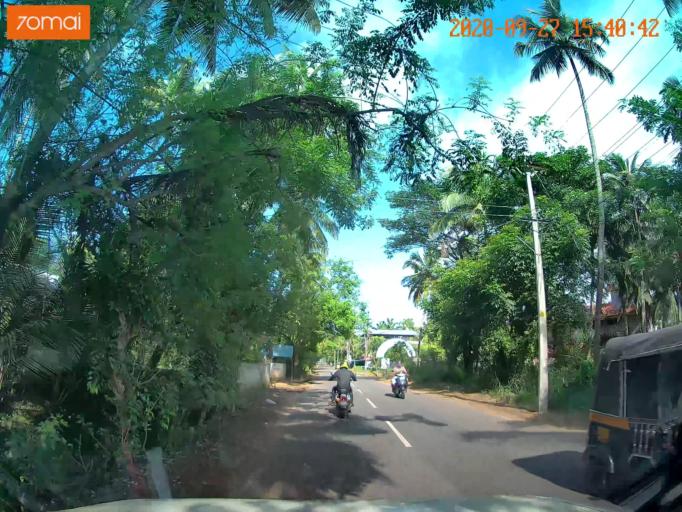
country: IN
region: Kerala
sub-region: Thrissur District
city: Thanniyam
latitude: 10.4703
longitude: 76.0885
